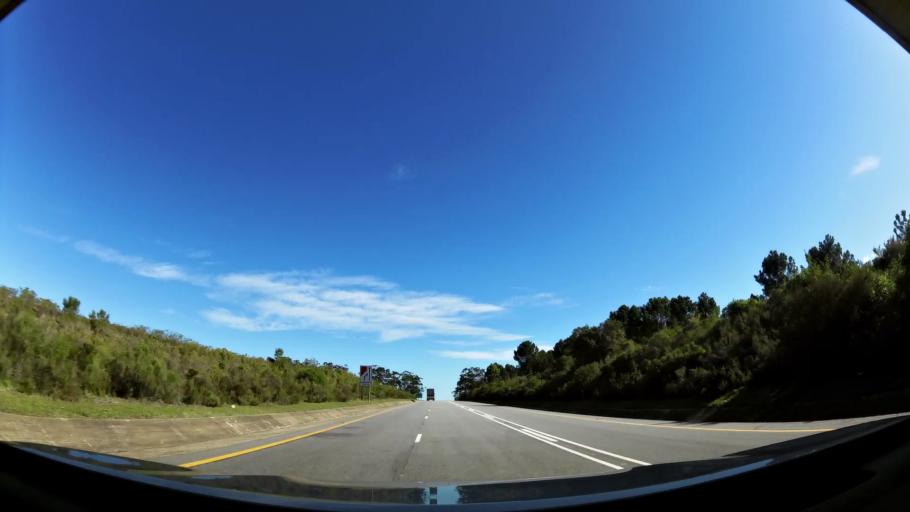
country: ZA
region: Eastern Cape
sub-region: Cacadu District Municipality
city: Kruisfontein
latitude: -34.0190
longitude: 24.6206
